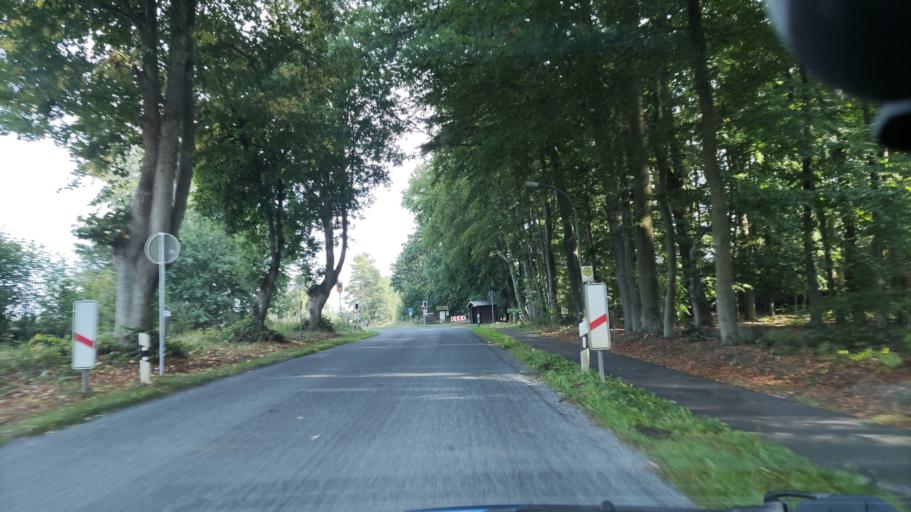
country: DE
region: Lower Saxony
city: Munster
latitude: 52.9781
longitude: 10.1376
